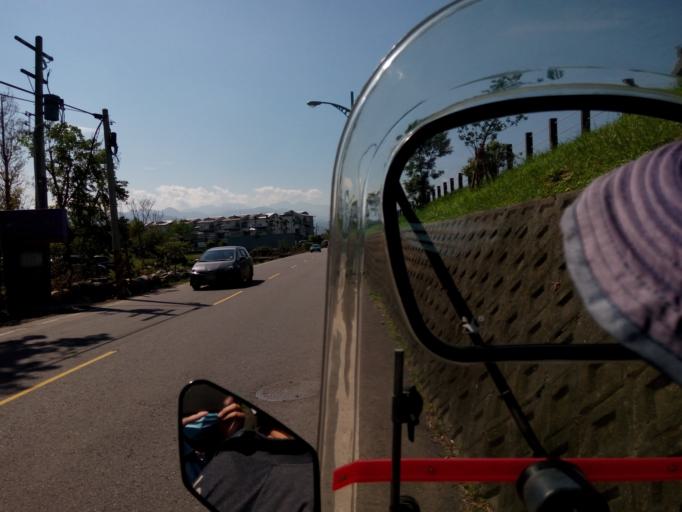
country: TW
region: Taiwan
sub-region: Yilan
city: Yilan
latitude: 24.6750
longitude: 121.7432
